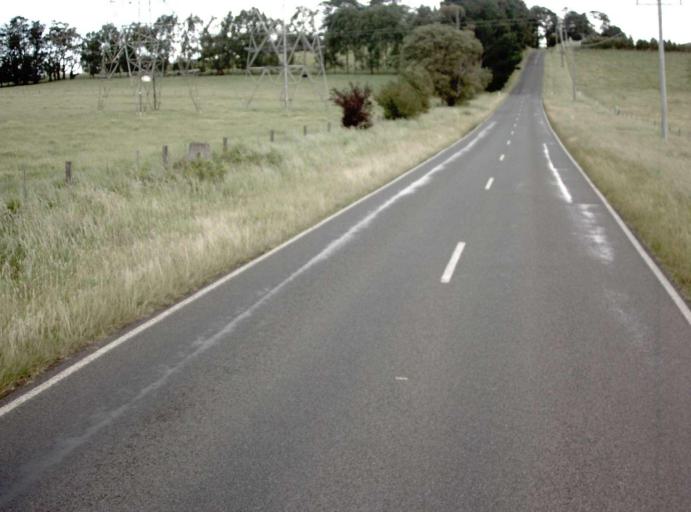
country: AU
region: Victoria
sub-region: Baw Baw
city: Warragul
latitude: -38.1070
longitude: 145.9244
